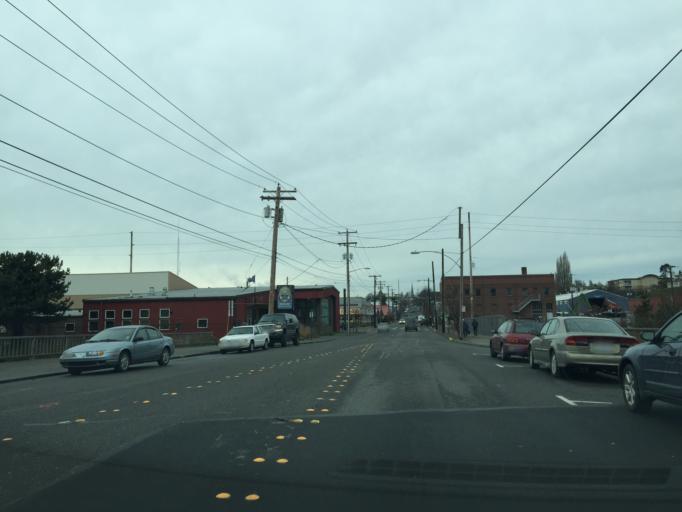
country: US
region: Washington
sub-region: Whatcom County
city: Bellingham
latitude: 48.7530
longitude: -122.4841
